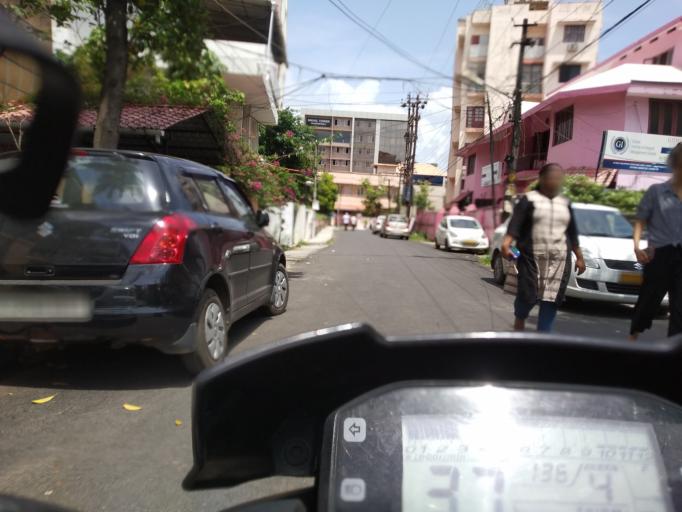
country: IN
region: Kerala
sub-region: Ernakulam
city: Cochin
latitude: 9.9840
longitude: 76.2855
